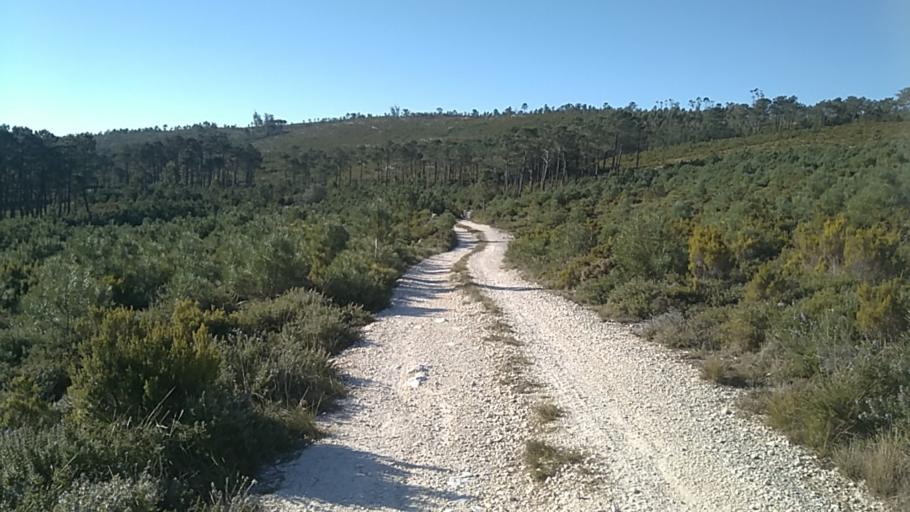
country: PT
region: Leiria
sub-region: Alcobaca
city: Aljubarrota
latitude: 39.5403
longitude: -8.8603
